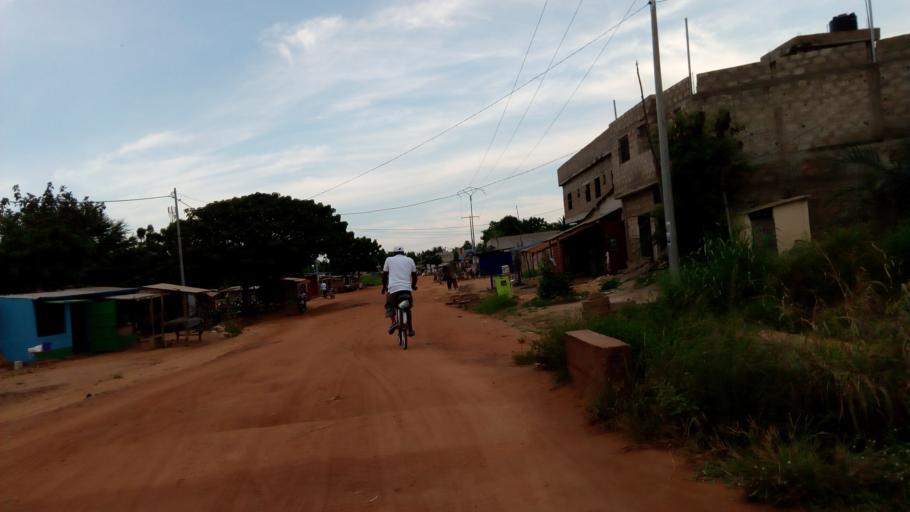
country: TG
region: Maritime
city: Lome
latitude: 6.2499
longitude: 1.1399
